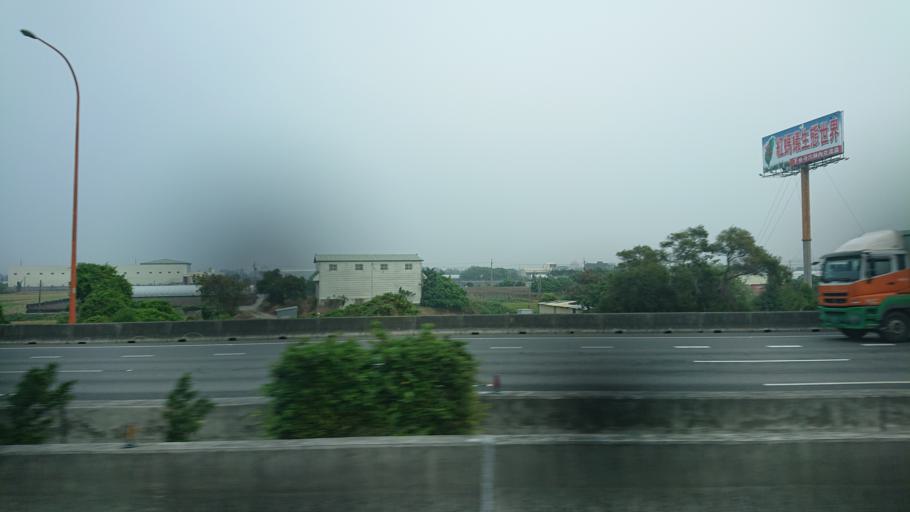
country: TW
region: Taiwan
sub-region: Changhua
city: Chang-hua
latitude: 23.9608
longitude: 120.5064
